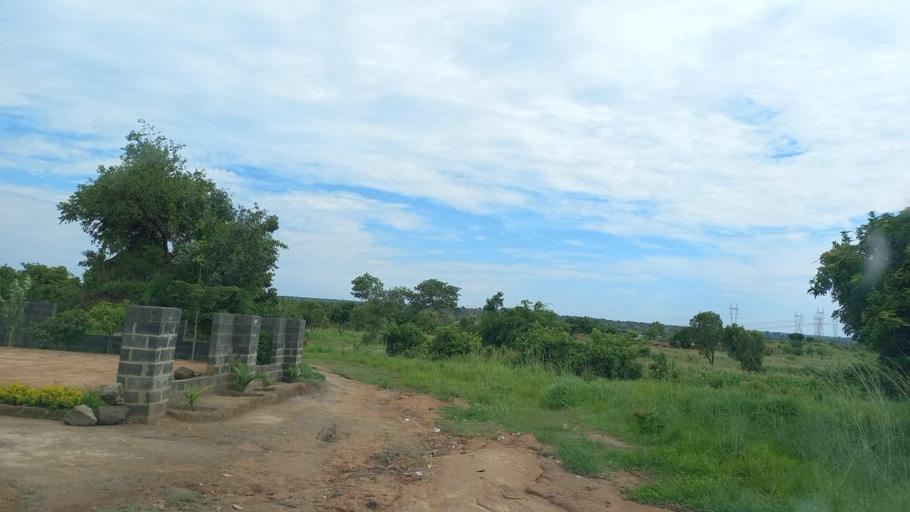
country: ZM
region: Copperbelt
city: Kitwe
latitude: -12.8670
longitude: 28.3351
